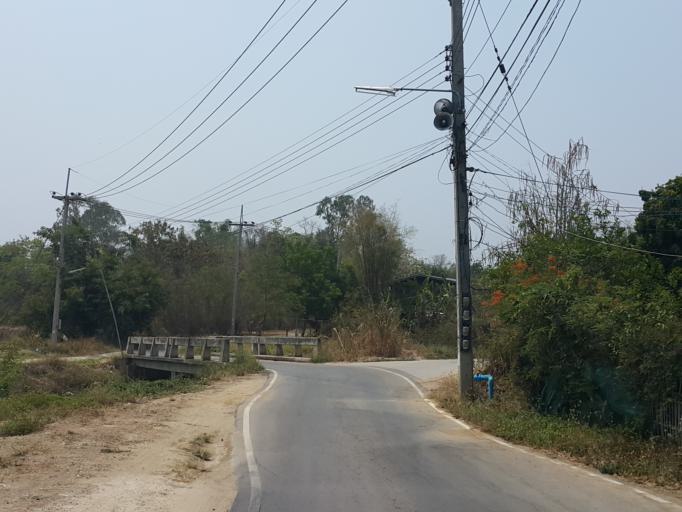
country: TH
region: Chiang Mai
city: San Kamphaeng
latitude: 18.7204
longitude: 99.1744
